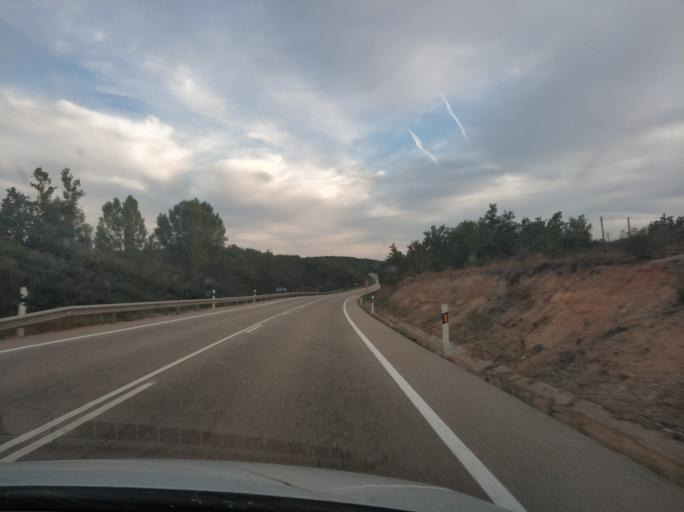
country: ES
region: Castille and Leon
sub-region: Provincia de Burgos
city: Pinilla de los Barruecos
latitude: 41.9233
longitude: -3.2792
